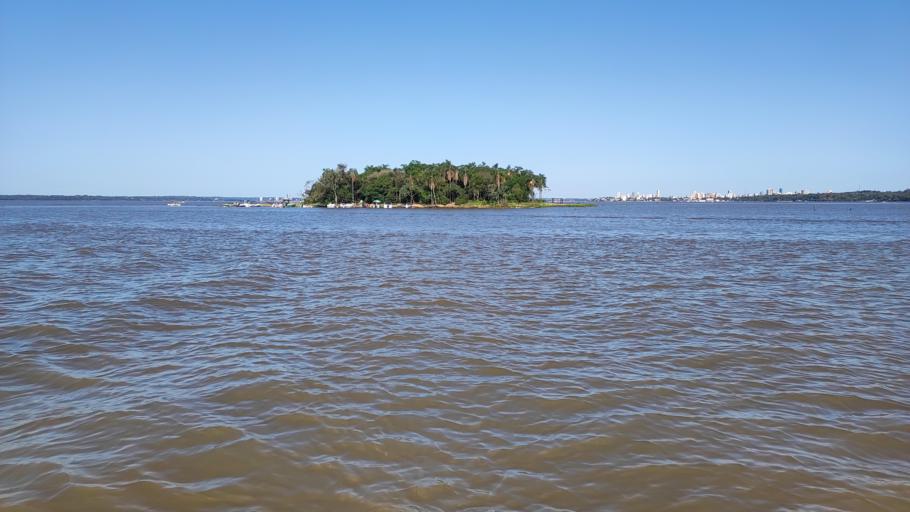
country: PY
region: Itapua
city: San Juan del Parana
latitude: -27.3403
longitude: -55.9527
